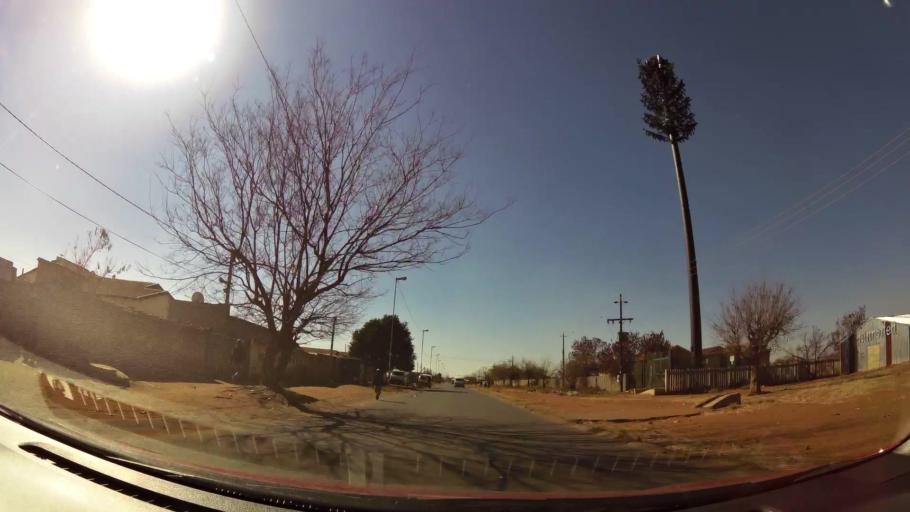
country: ZA
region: Gauteng
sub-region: City of Johannesburg Metropolitan Municipality
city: Soweto
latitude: -26.2246
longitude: 27.8275
